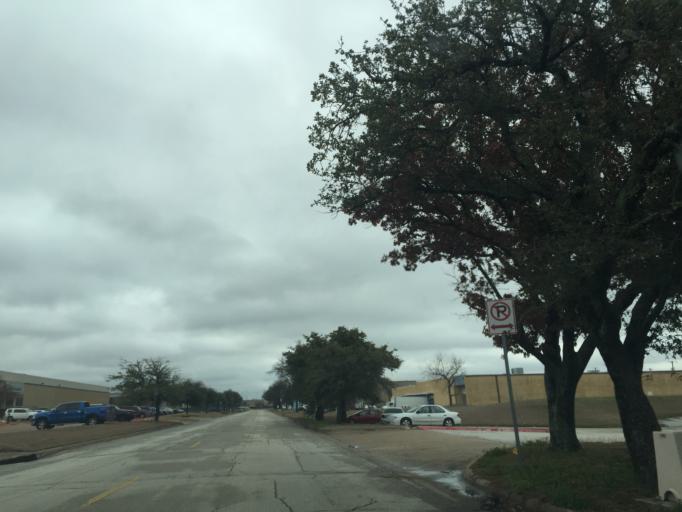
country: US
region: Texas
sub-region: Tarrant County
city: Arlington
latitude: 32.7526
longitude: -97.0574
